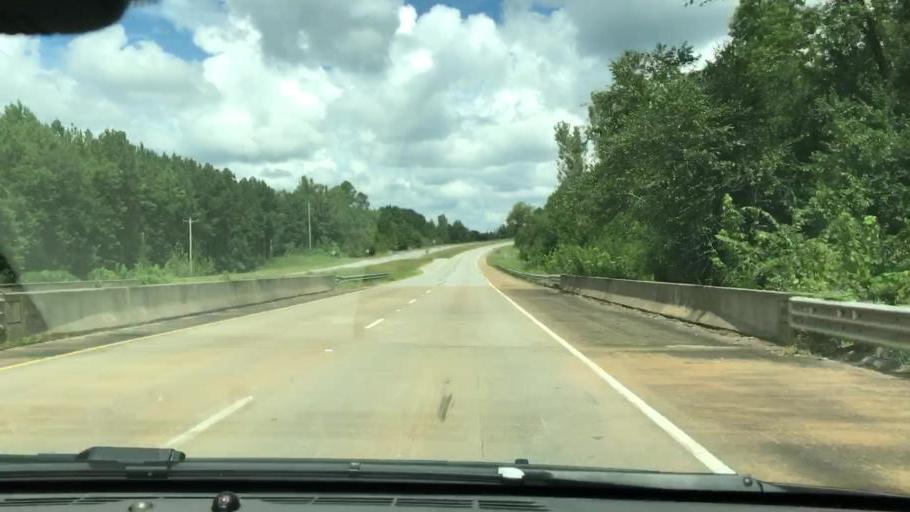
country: US
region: Georgia
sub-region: Stewart County
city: Lumpkin
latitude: 32.1029
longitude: -84.8118
